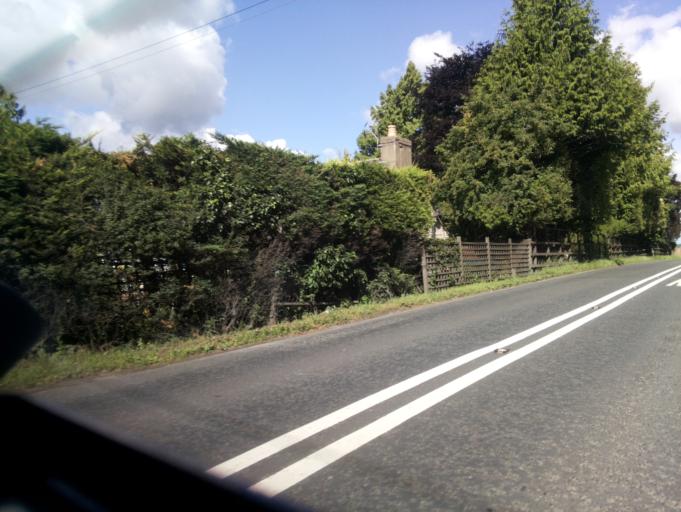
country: GB
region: England
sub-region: Gloucestershire
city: Newent
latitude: 51.9106
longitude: -2.3426
